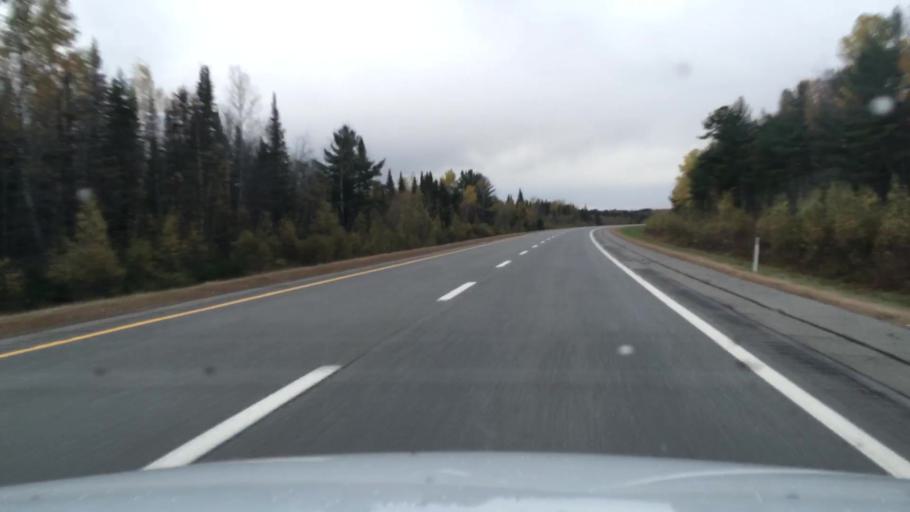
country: US
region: Maine
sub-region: Penobscot County
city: Greenbush
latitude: 45.1196
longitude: -68.6950
